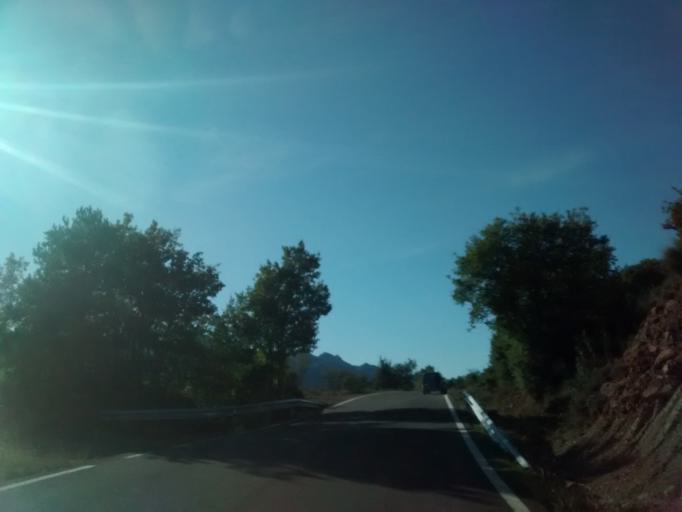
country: ES
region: Aragon
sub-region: Provincia de Zaragoza
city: Santa Eulalia de Gallego
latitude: 42.3926
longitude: -0.7276
